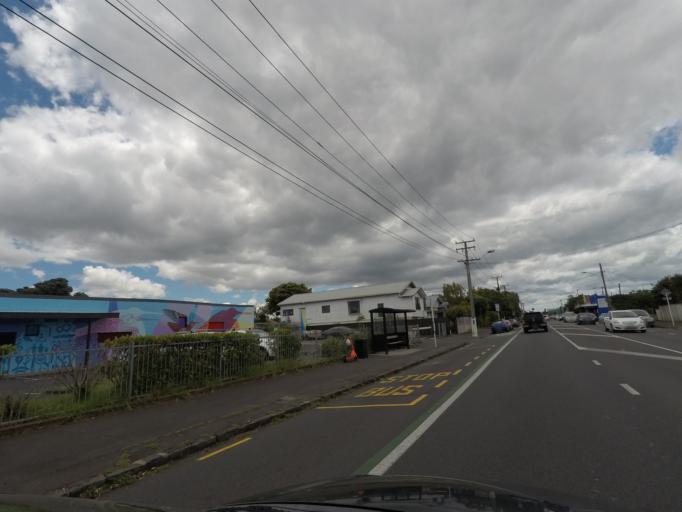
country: NZ
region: Auckland
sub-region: Auckland
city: Auckland
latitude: -36.8874
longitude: 174.7376
